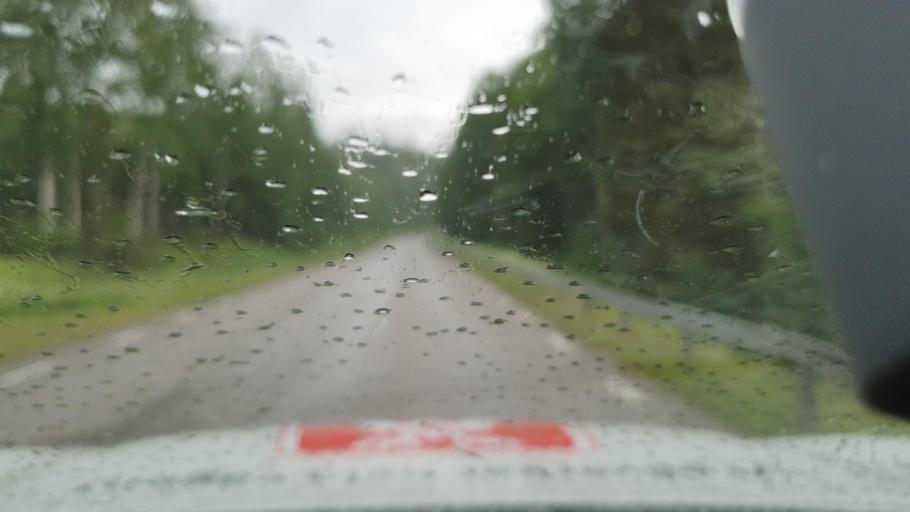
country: SE
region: Vaesterbotten
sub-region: Vannas Kommun
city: Vaennaes
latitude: 63.7897
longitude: 19.5626
